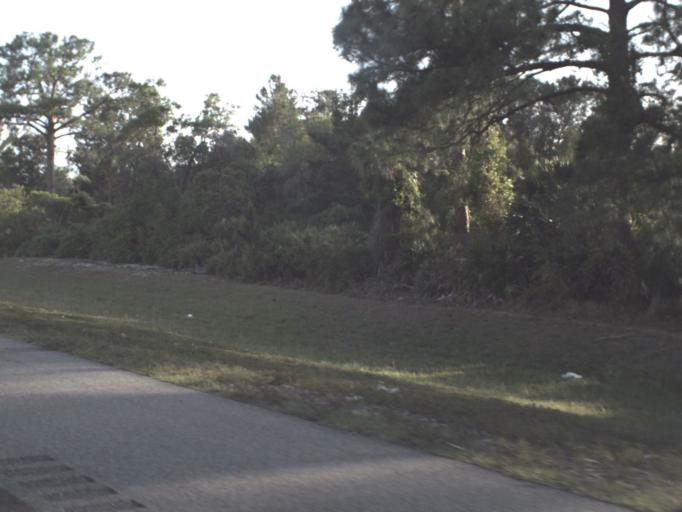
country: US
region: Florida
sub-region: Brevard County
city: Titusville
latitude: 28.5890
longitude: -80.8515
